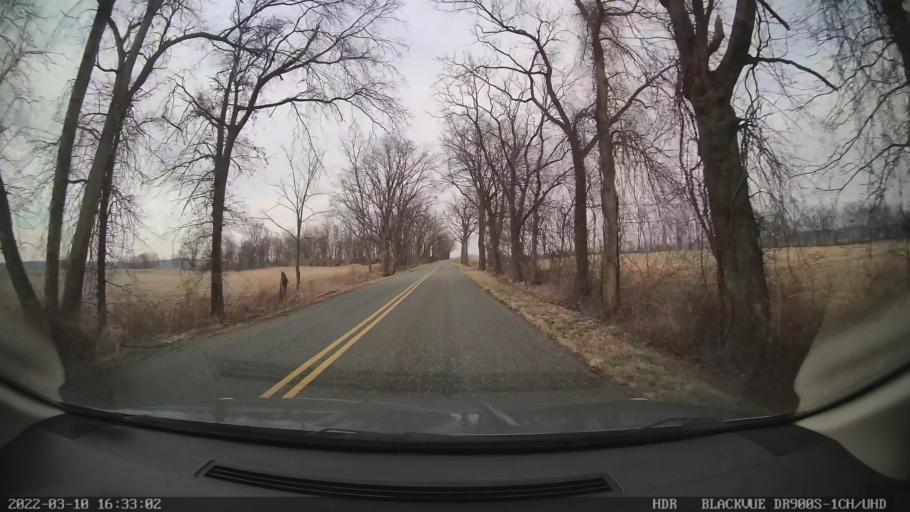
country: US
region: Pennsylvania
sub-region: Berks County
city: Oley
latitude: 40.3675
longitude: -75.7863
